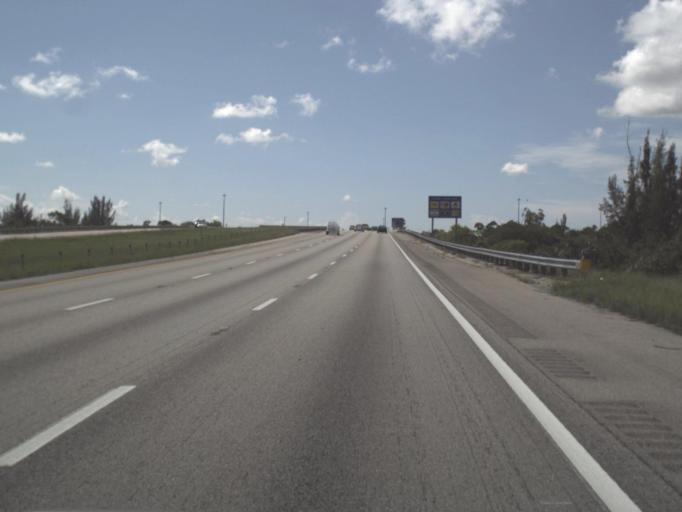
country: US
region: Florida
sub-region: Charlotte County
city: Punta Gorda
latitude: 26.9452
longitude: -82.0206
